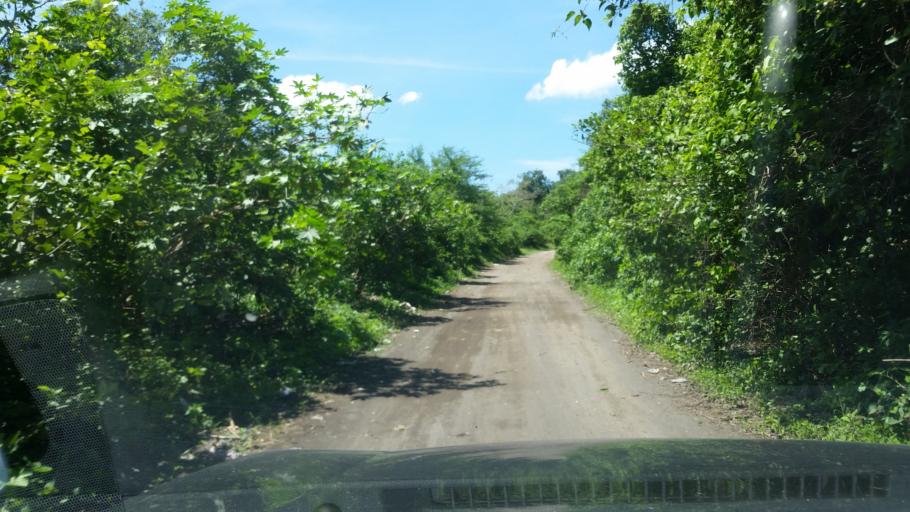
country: NI
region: Chinandega
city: Puerto Morazan
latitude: 12.7638
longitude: -87.1336
